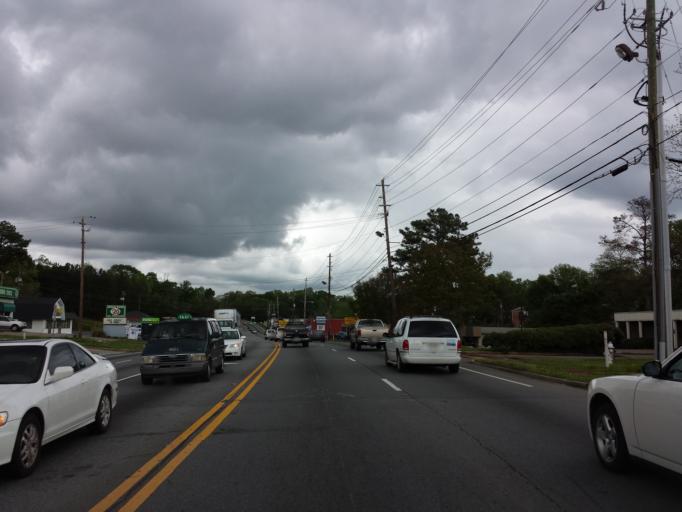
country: US
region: Georgia
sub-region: Cobb County
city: Marietta
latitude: 33.9362
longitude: -84.5558
